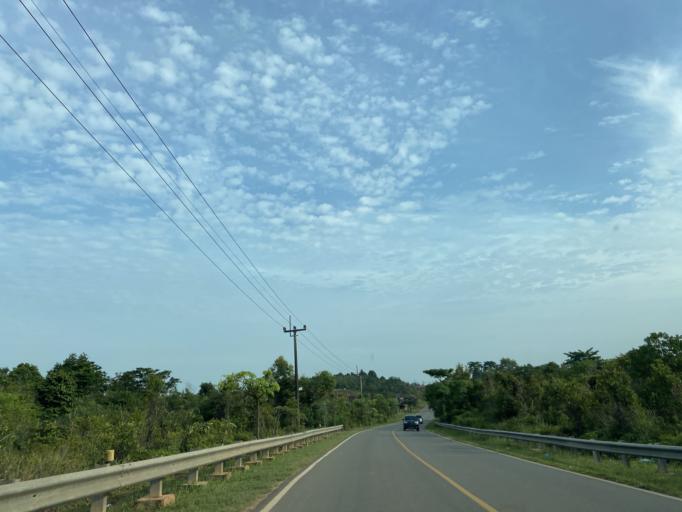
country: ID
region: Riau Islands
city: Tanjungpinang
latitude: 0.9063
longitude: 104.1246
